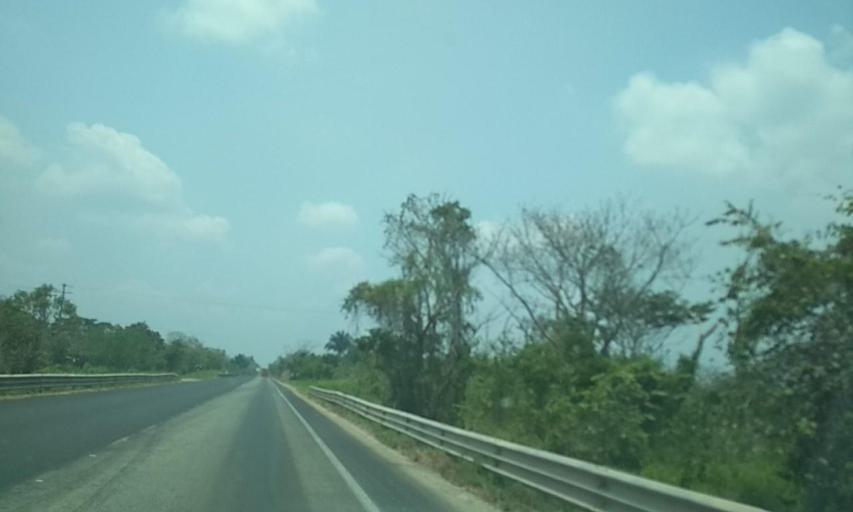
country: MX
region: Tabasco
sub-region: Huimanguillo
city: Francisco Rueda
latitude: 17.7195
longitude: -93.9525
